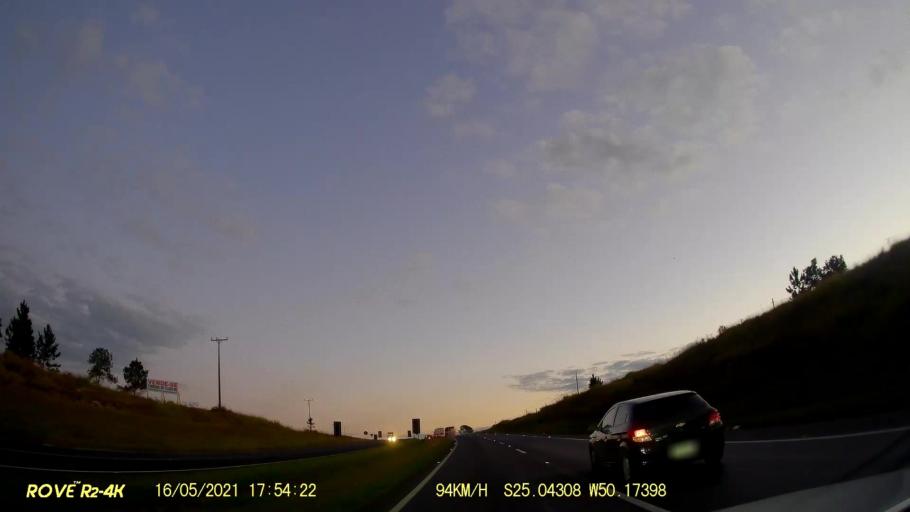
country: BR
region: Parana
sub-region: Ponta Grossa
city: Ponta Grossa
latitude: -25.0437
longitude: -50.1741
